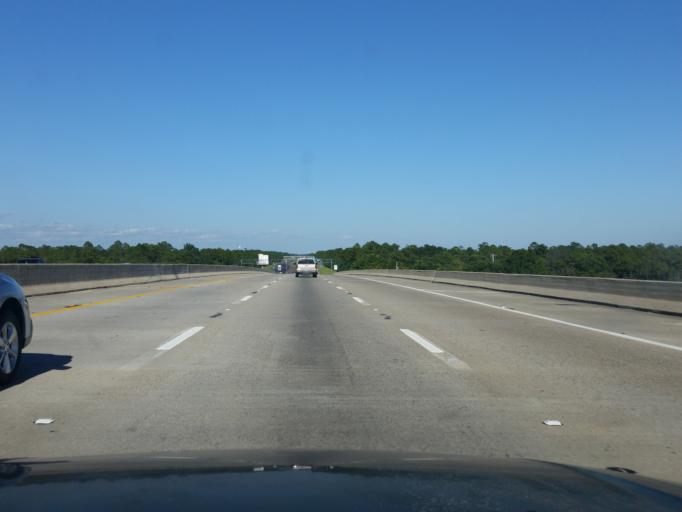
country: US
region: Mississippi
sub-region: Hancock County
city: Diamondhead
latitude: 30.3652
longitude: -89.4007
